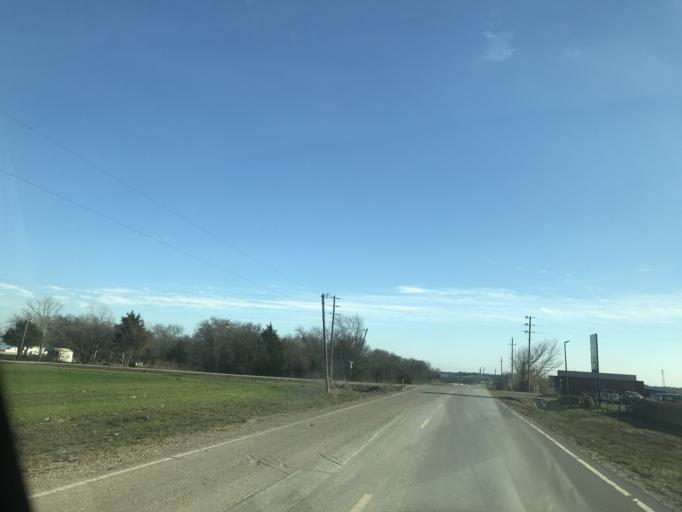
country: US
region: Texas
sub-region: Dallas County
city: Wilmer
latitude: 32.5666
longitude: -96.6696
